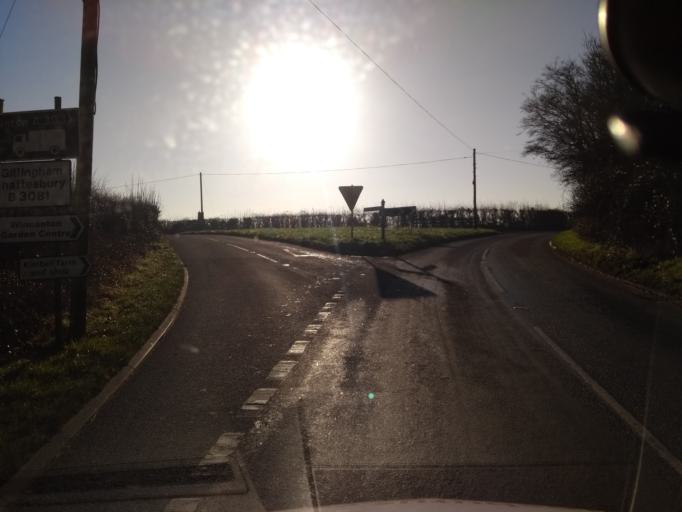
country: GB
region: England
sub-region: Somerset
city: Redlynch
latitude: 51.0866
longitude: -2.4132
